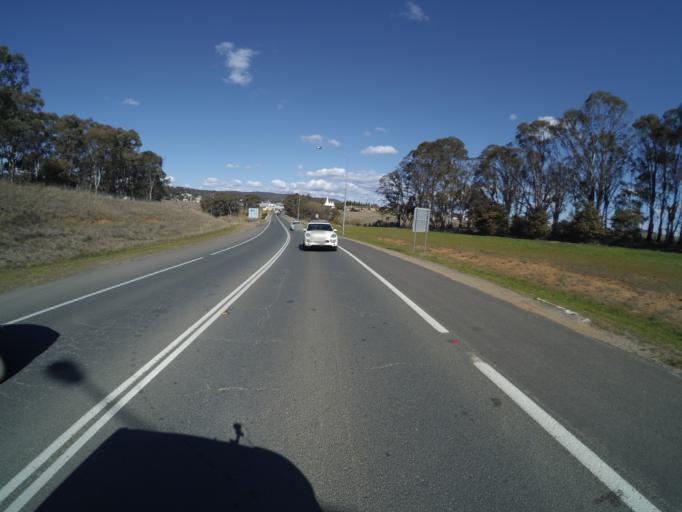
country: AU
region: New South Wales
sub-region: Queanbeyan
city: Queanbeyan
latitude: -35.3342
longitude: 149.2391
